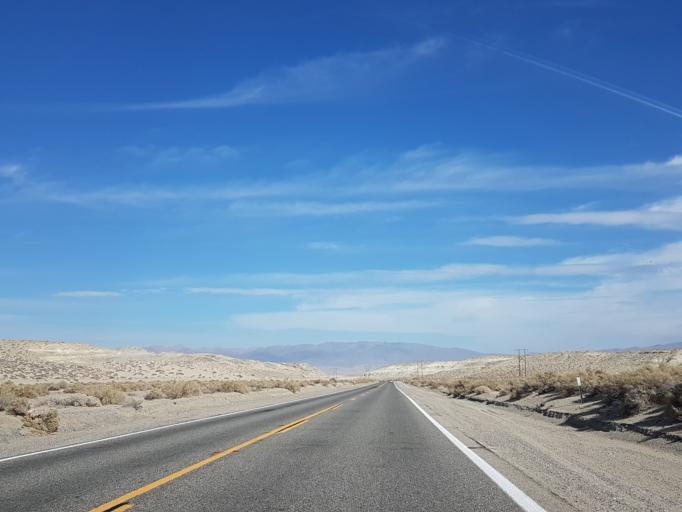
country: US
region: California
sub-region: San Bernardino County
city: Searles Valley
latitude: 35.6688
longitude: -117.4228
